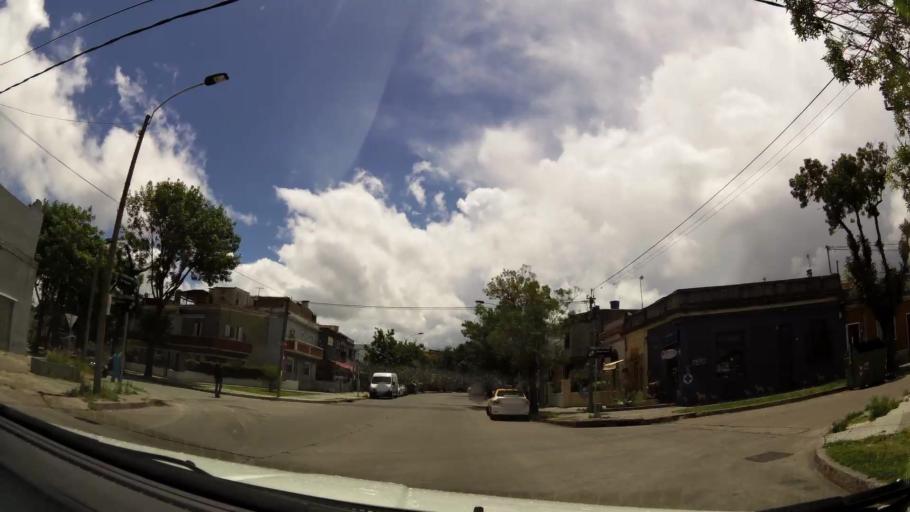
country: UY
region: Montevideo
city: Montevideo
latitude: -34.8630
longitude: -56.1869
